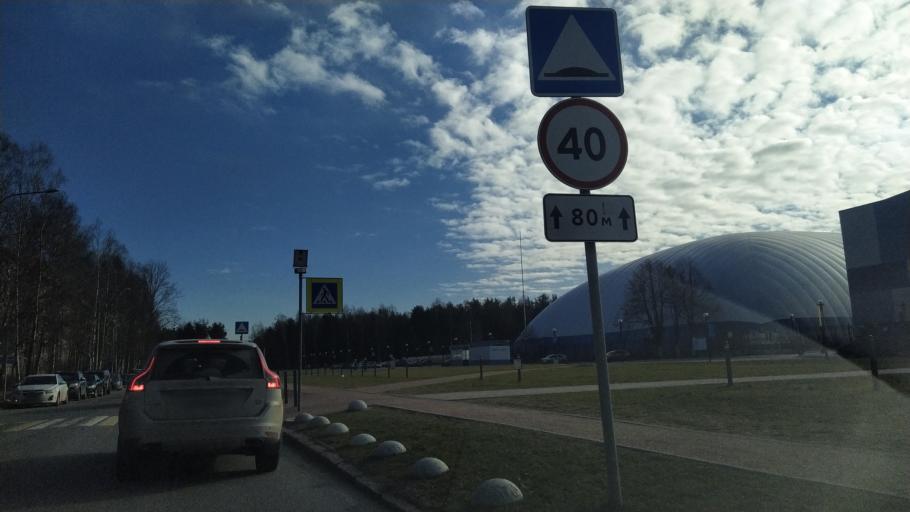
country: RU
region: Leningrad
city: Akademicheskoe
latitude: 60.0046
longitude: 30.4115
